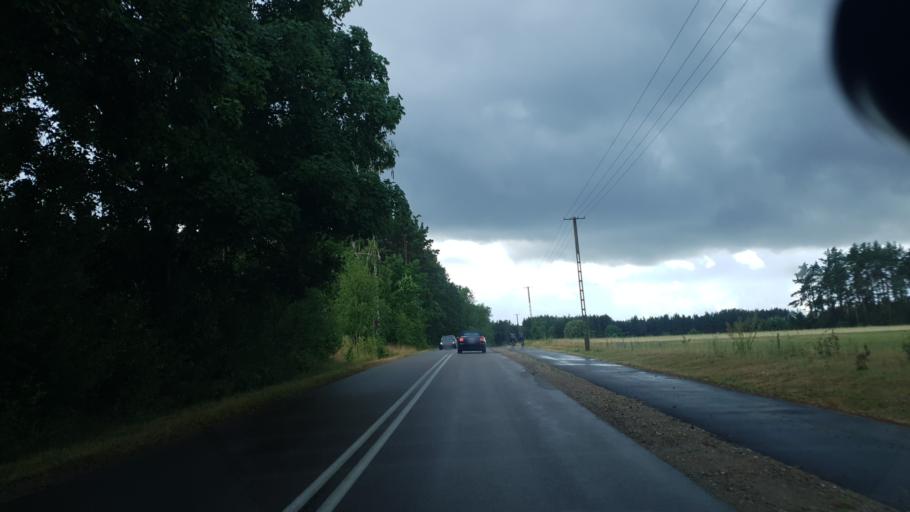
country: PL
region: Pomeranian Voivodeship
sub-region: Powiat kartuski
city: Stezyca
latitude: 54.2271
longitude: 17.9730
